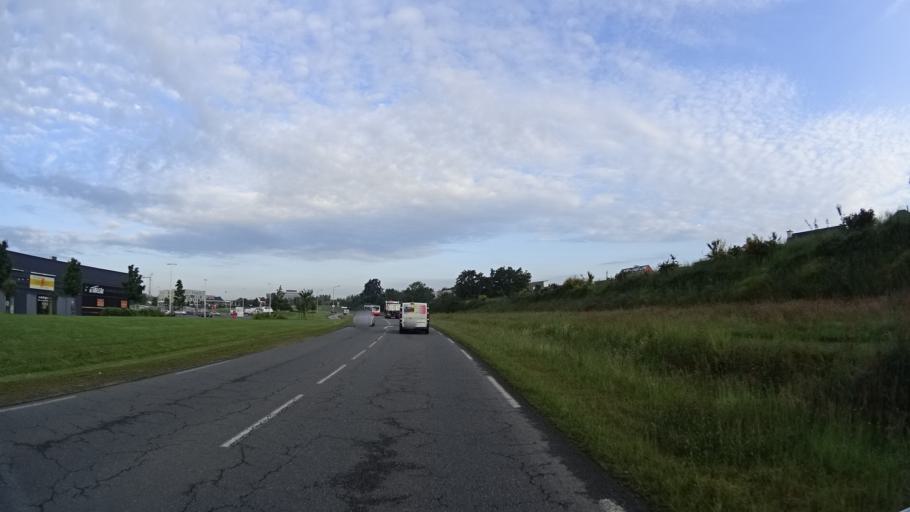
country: FR
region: Brittany
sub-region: Departement du Morbihan
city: Sene
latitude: 47.6437
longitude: -2.7387
